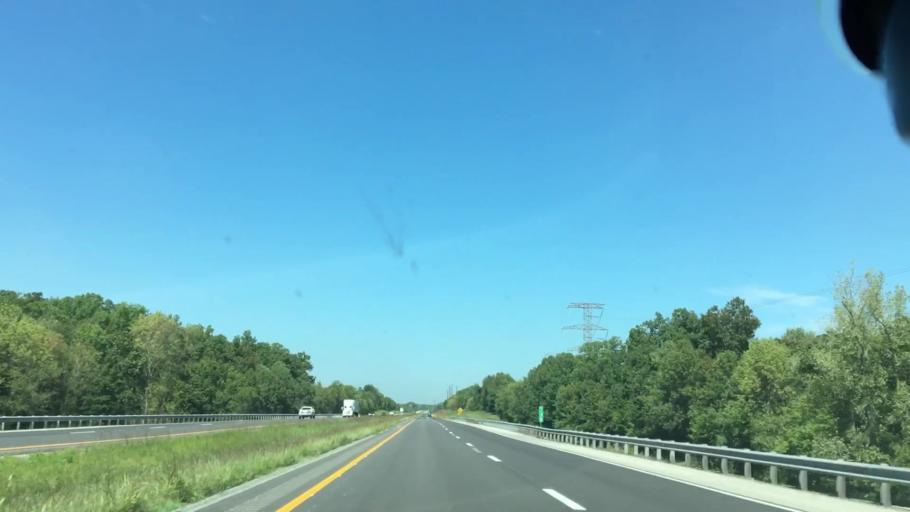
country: US
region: Kentucky
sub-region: Webster County
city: Sebree
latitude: 37.6296
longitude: -87.5086
